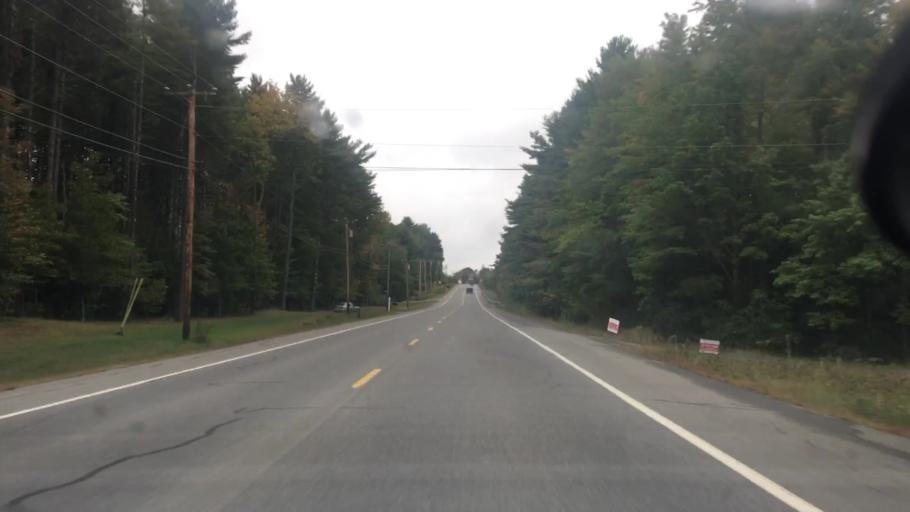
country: US
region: Maine
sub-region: Kennebec County
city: Belgrade
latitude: 44.4016
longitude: -69.8098
